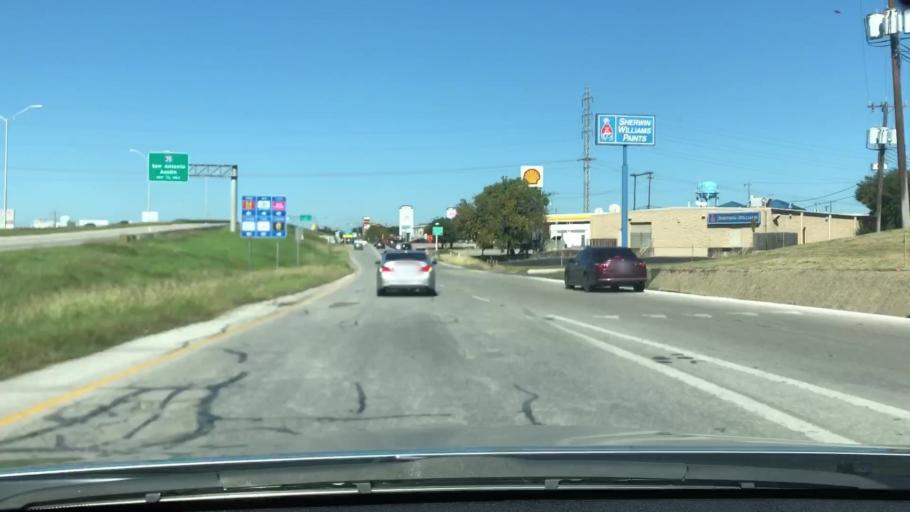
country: US
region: Texas
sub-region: Bexar County
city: Live Oak
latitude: 29.5583
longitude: -98.3252
